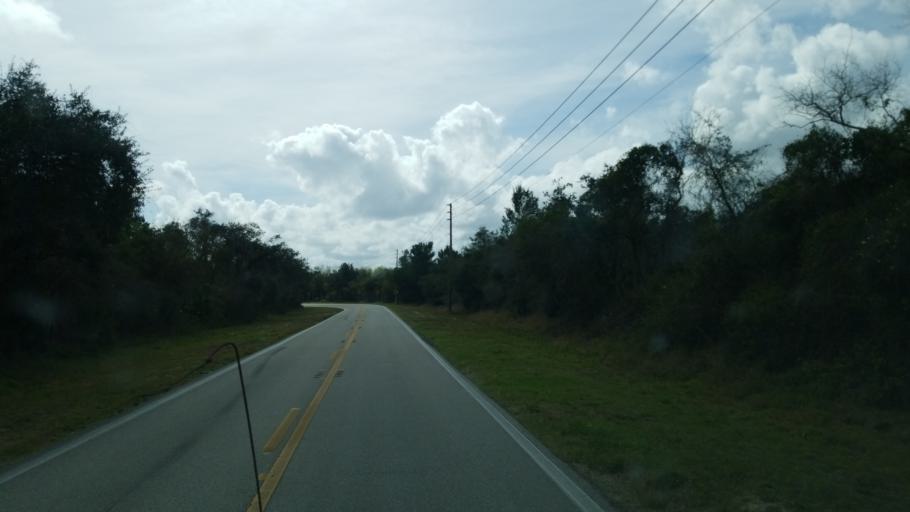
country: US
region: Florida
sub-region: Polk County
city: Dundee
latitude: 28.0584
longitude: -81.5433
